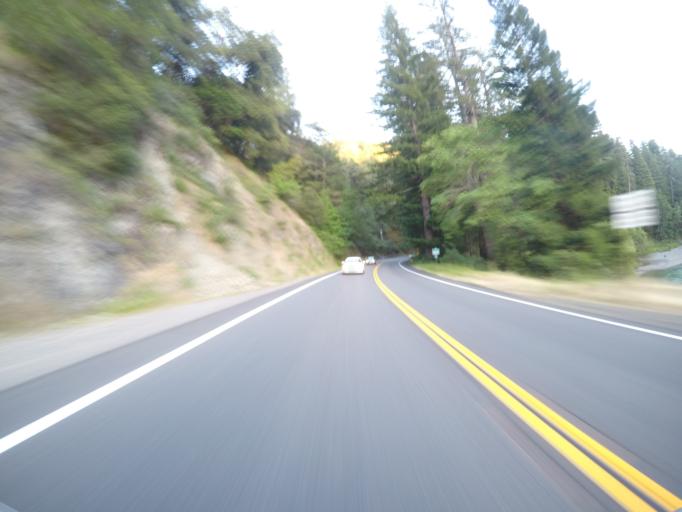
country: US
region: California
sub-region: Humboldt County
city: Redway
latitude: 39.8996
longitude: -123.7520
